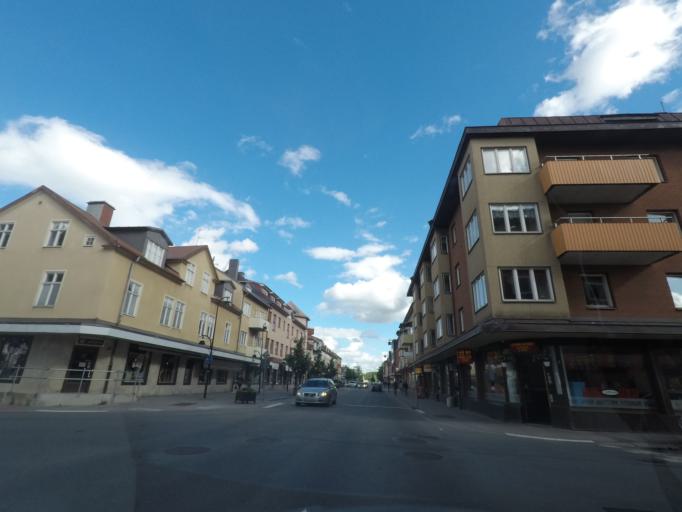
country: SE
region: OErebro
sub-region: Lindesbergs Kommun
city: Lindesberg
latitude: 59.5937
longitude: 15.2273
